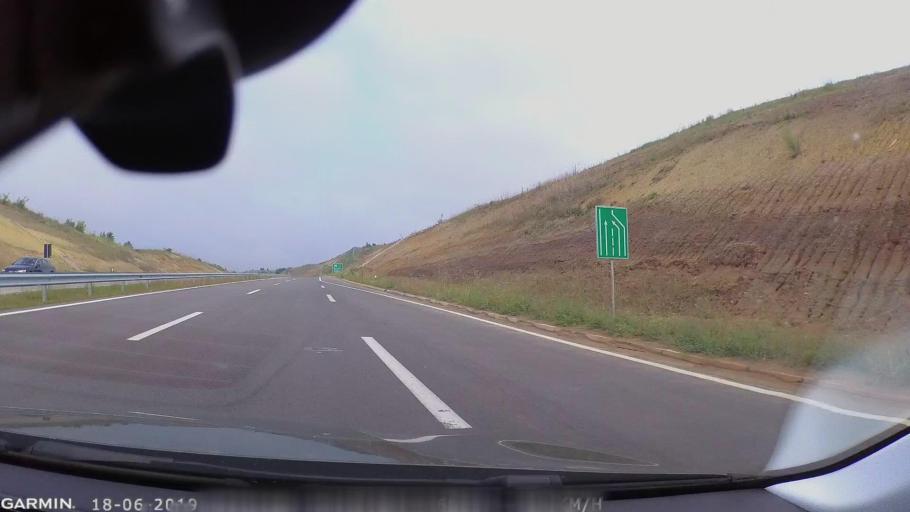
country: MK
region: Petrovec
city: Sredno Konjare
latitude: 41.9464
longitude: 21.7807
